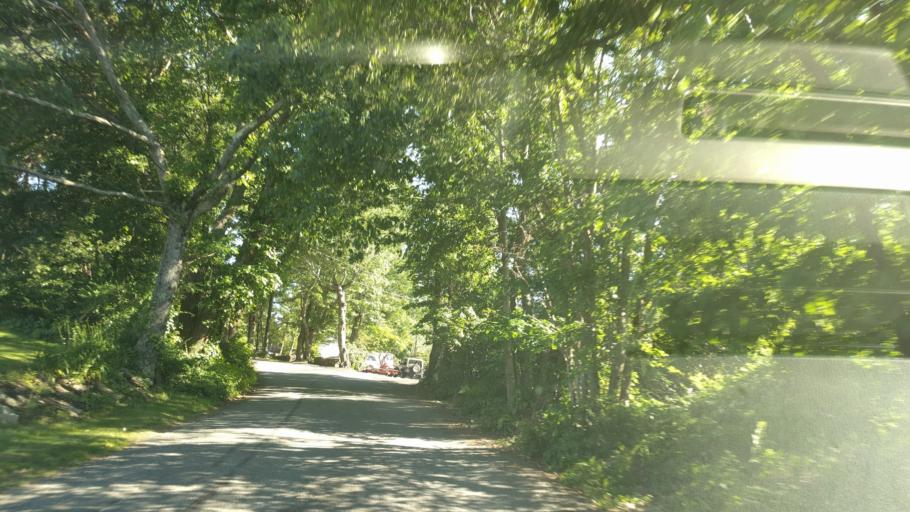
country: US
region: Massachusetts
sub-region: Worcester County
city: Oxford
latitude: 42.1401
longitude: -71.8362
